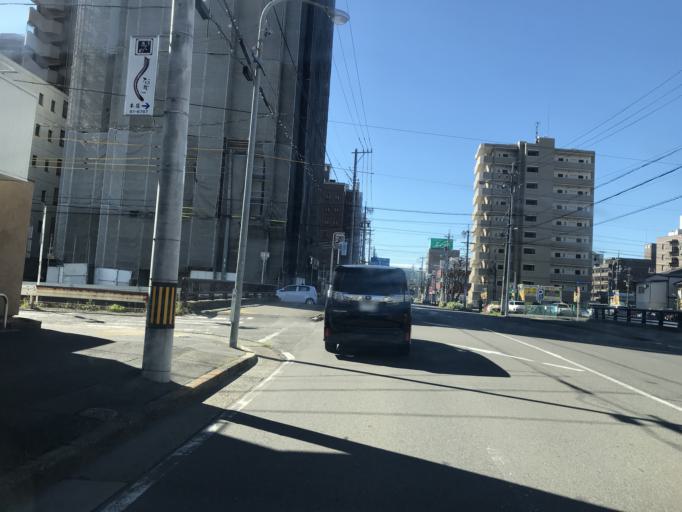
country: JP
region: Aichi
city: Kasugai
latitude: 35.2457
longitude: 136.9838
